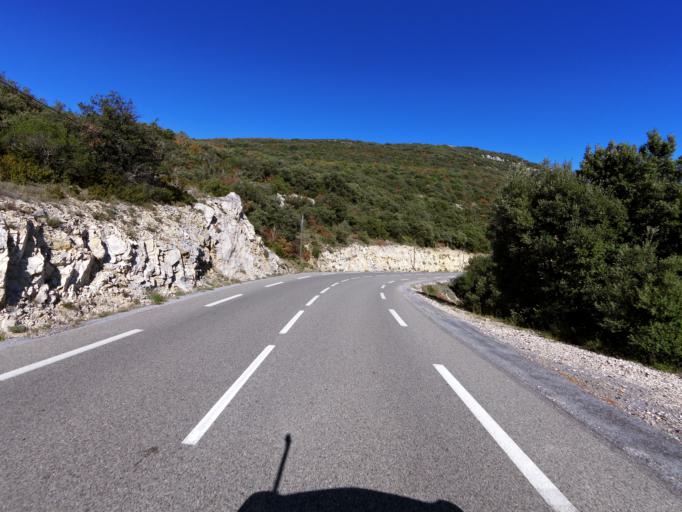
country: FR
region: Languedoc-Roussillon
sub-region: Departement du Gard
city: Saint-Julien-de-Peyrolas
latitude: 44.4001
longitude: 4.4756
